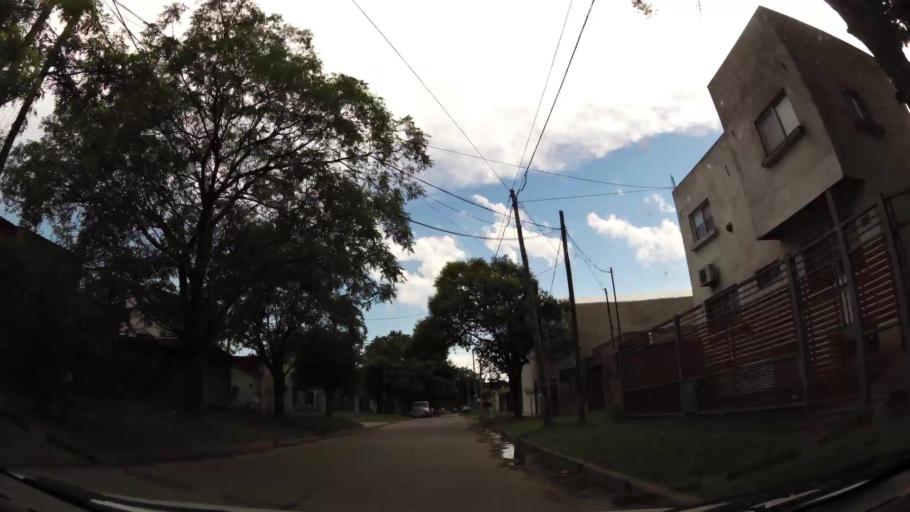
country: AR
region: Buenos Aires
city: Ituzaingo
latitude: -34.6322
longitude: -58.6941
